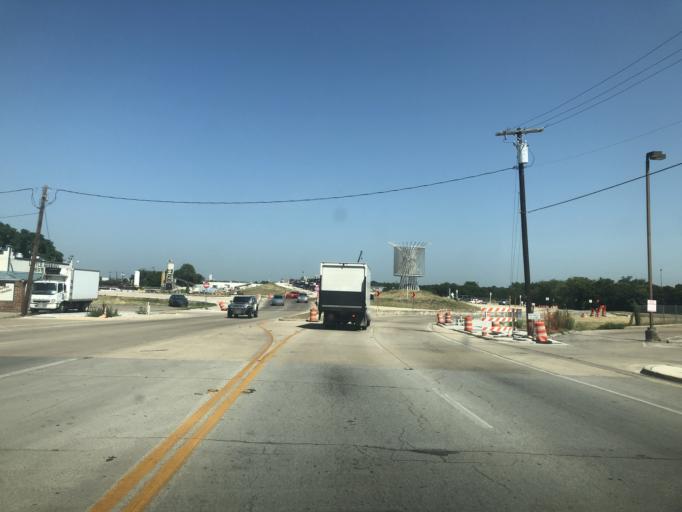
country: US
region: Texas
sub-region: Tarrant County
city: Fort Worth
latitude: 32.7592
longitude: -97.3437
